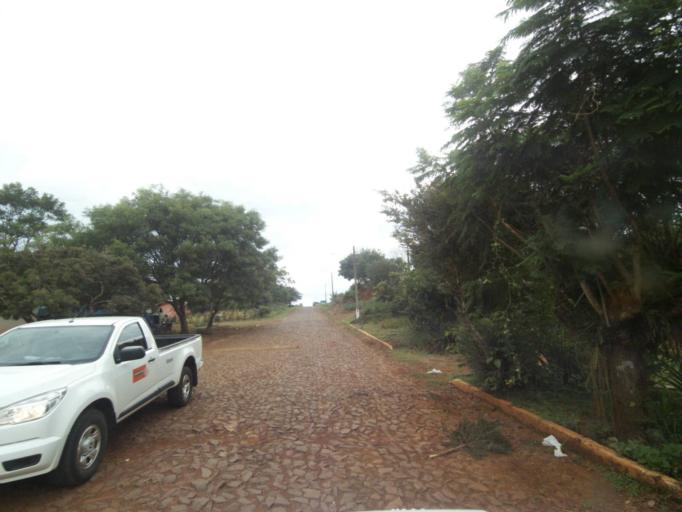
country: BR
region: Parana
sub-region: Guaraniacu
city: Guaraniacu
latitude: -24.9220
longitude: -52.9377
